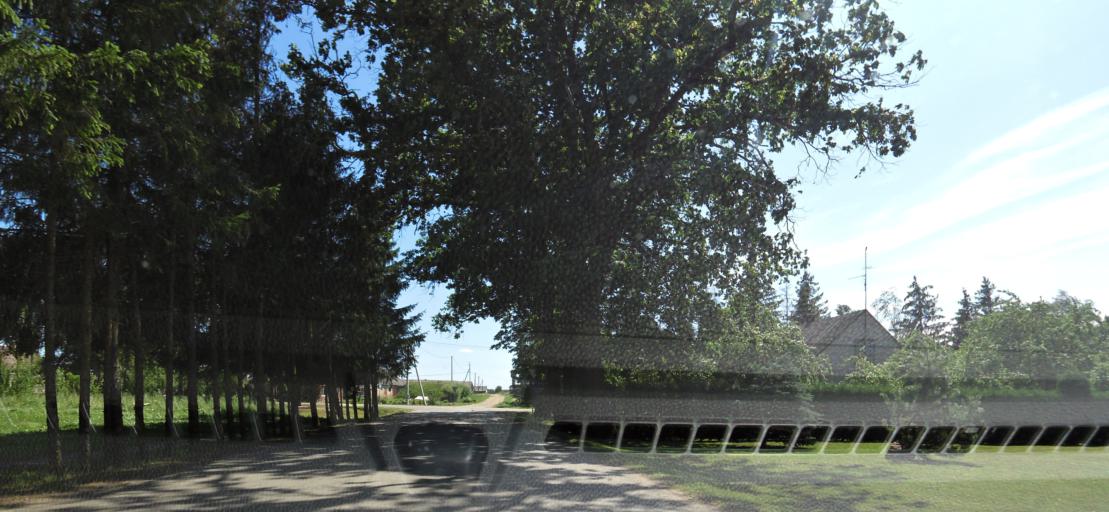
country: LT
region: Panevezys
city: Pasvalys
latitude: 56.2510
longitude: 24.3610
